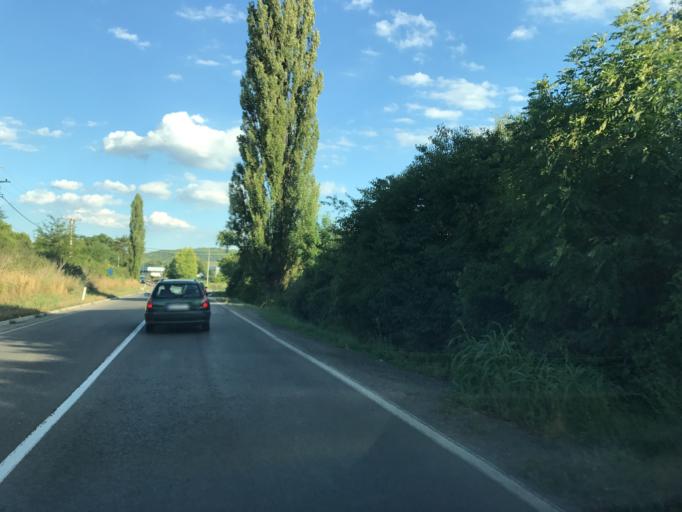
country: RS
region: Central Serbia
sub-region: Belgrade
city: Grocka
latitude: 44.7249
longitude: 20.6260
